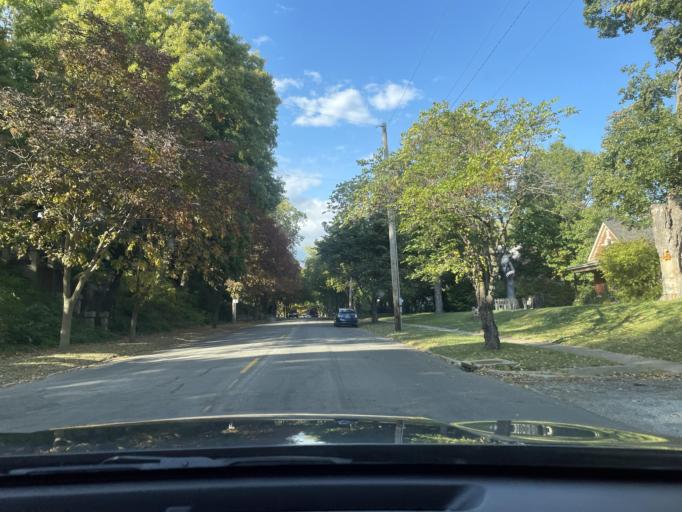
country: US
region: Missouri
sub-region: Buchanan County
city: Saint Joseph
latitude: 39.7840
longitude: -94.8343
